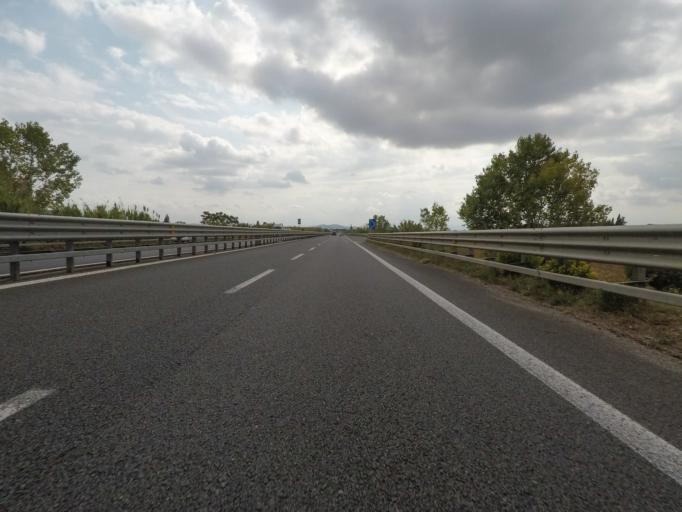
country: IT
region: Tuscany
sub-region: Provincia di Grosseto
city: Bagno Roselle
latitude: 42.8164
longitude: 11.1314
